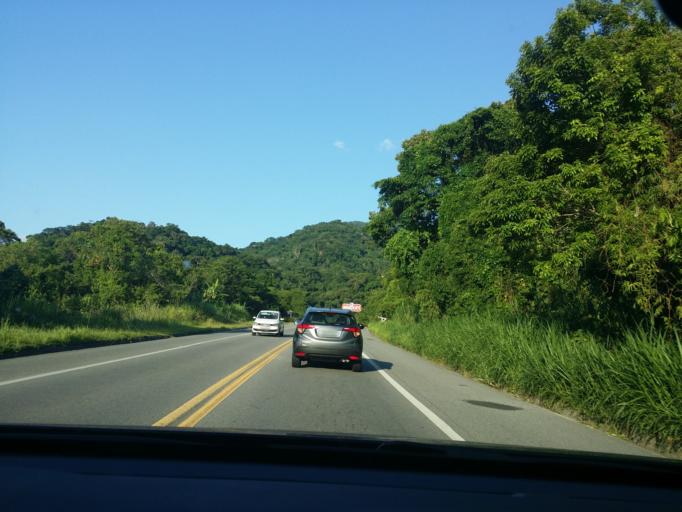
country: BR
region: Sao Paulo
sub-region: Sao Sebastiao
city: Sao Sebastiao
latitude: -23.7438
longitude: -45.7359
